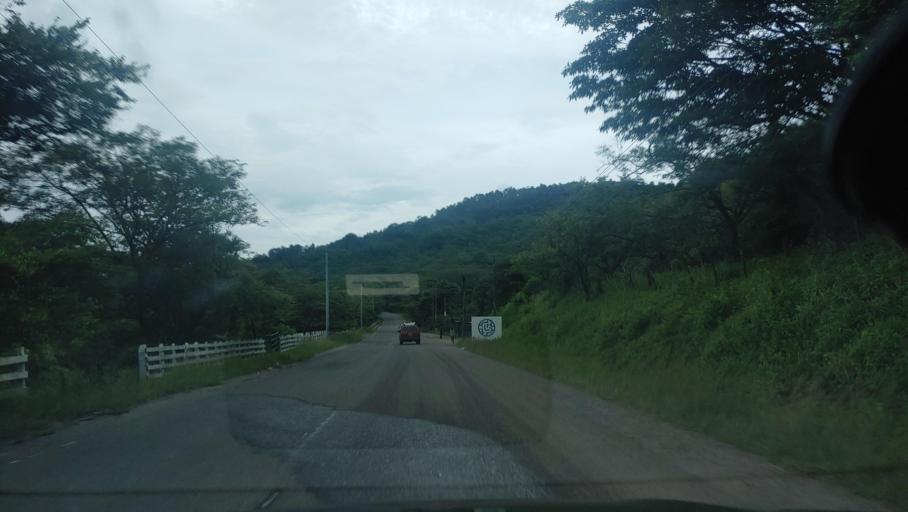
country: HN
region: Choluteca
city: San Marcos de Colon
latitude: 13.3807
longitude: -86.8706
